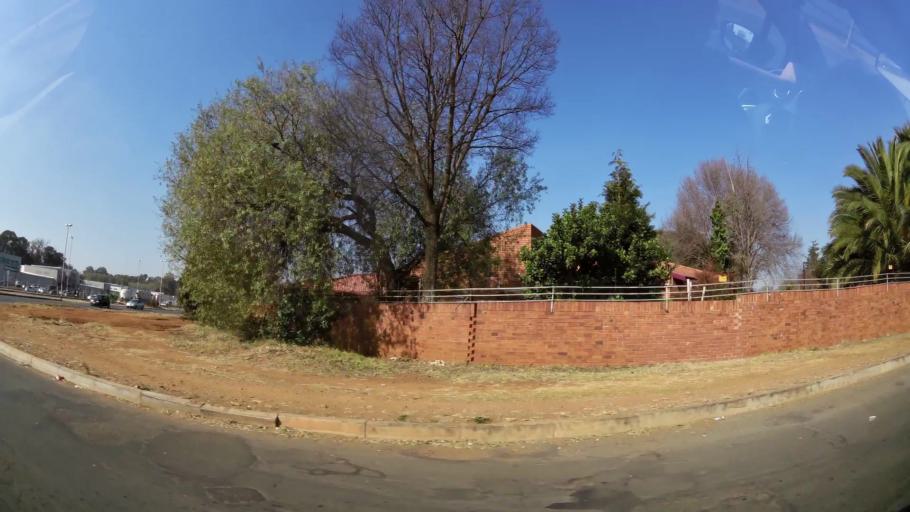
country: ZA
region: Gauteng
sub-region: West Rand District Municipality
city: Randfontein
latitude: -26.1733
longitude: 27.6895
